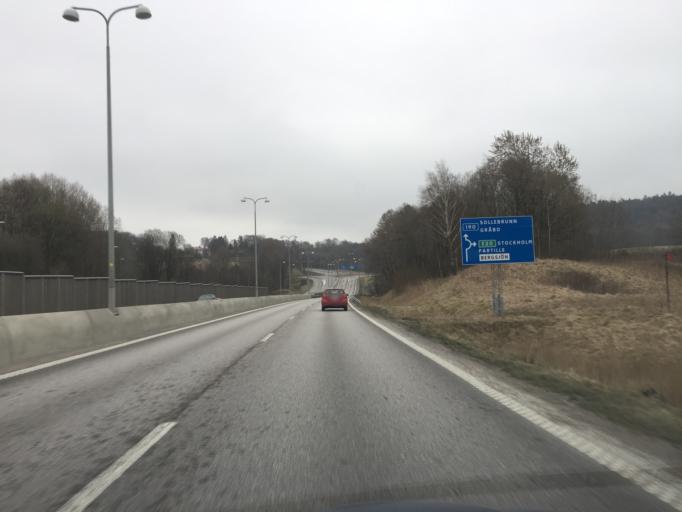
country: SE
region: Vaestra Goetaland
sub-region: Goteborg
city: Eriksbo
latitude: 57.7770
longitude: 12.0663
